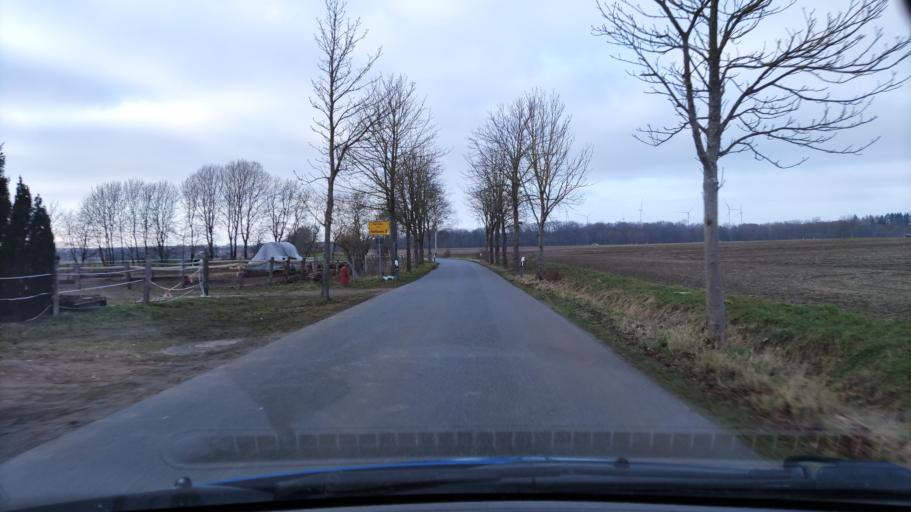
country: DE
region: Lower Saxony
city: Gerdau
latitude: 52.9553
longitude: 10.4256
